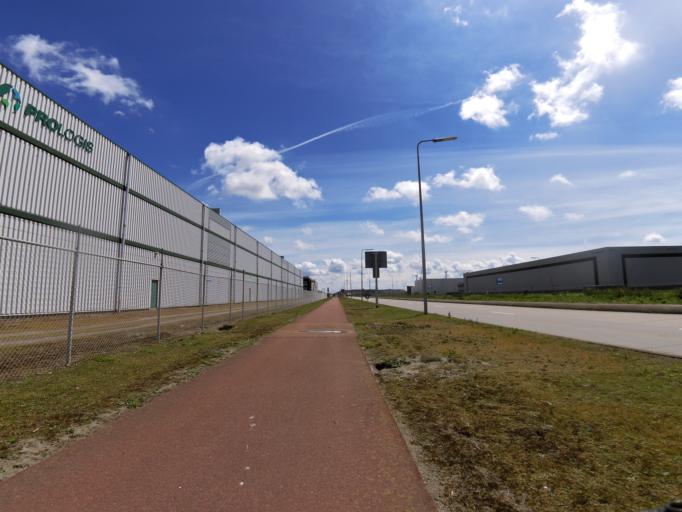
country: NL
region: South Holland
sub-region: Gemeente Rotterdam
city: Hoek van Holland
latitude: 51.9441
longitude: 4.0139
